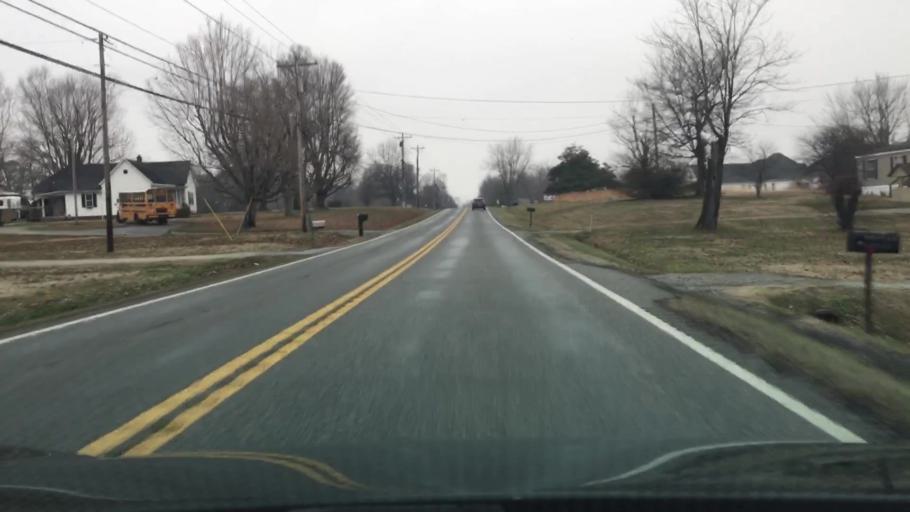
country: US
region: Kentucky
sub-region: Livingston County
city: Ledbetter
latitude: 36.9704
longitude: -88.4620
